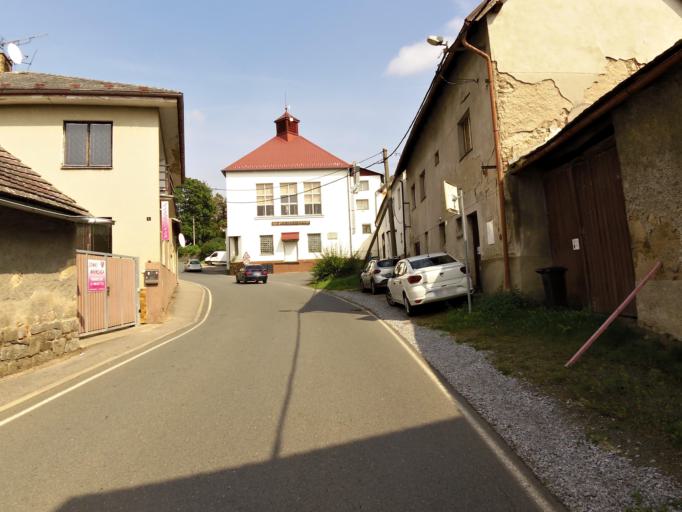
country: CZ
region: Central Bohemia
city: Tynec nad Sazavou
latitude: 49.8564
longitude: 14.5587
